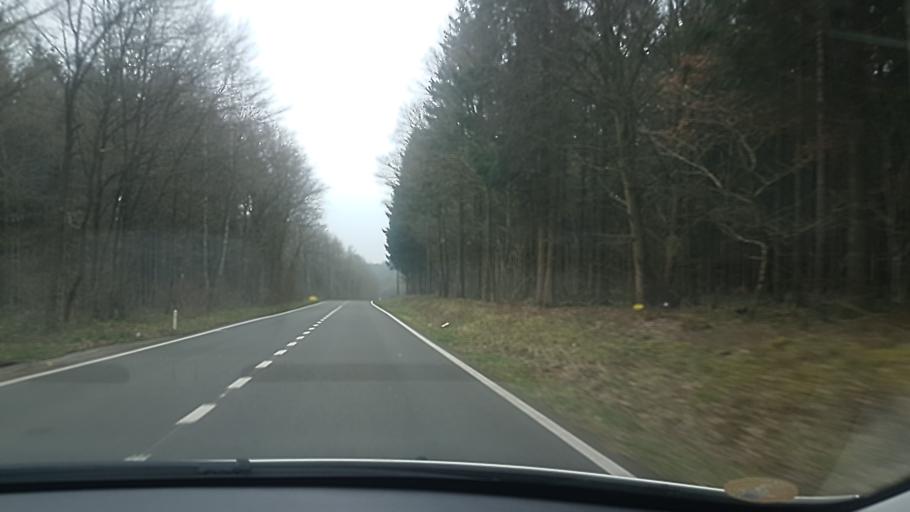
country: FR
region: Champagne-Ardenne
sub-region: Departement des Ardennes
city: Haybes
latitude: 50.0494
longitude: 4.6100
